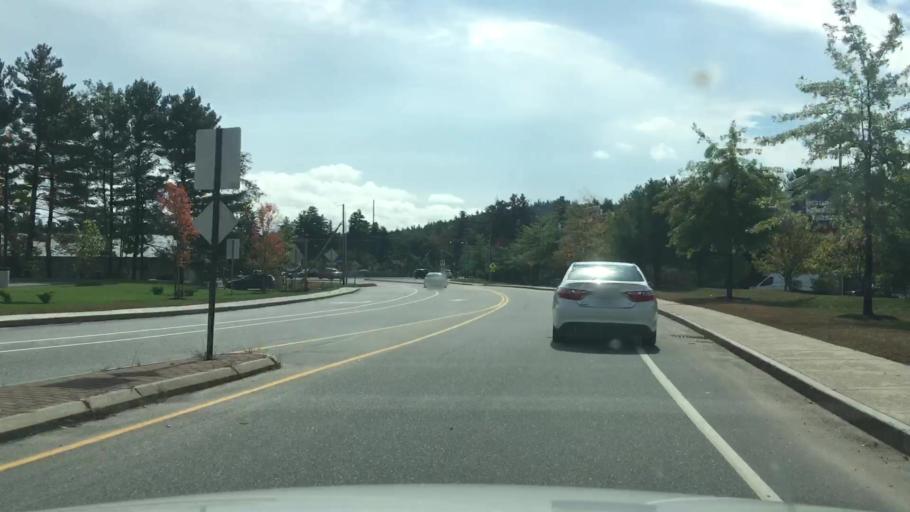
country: US
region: New Hampshire
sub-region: Carroll County
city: North Conway
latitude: 44.0196
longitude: -71.1097
